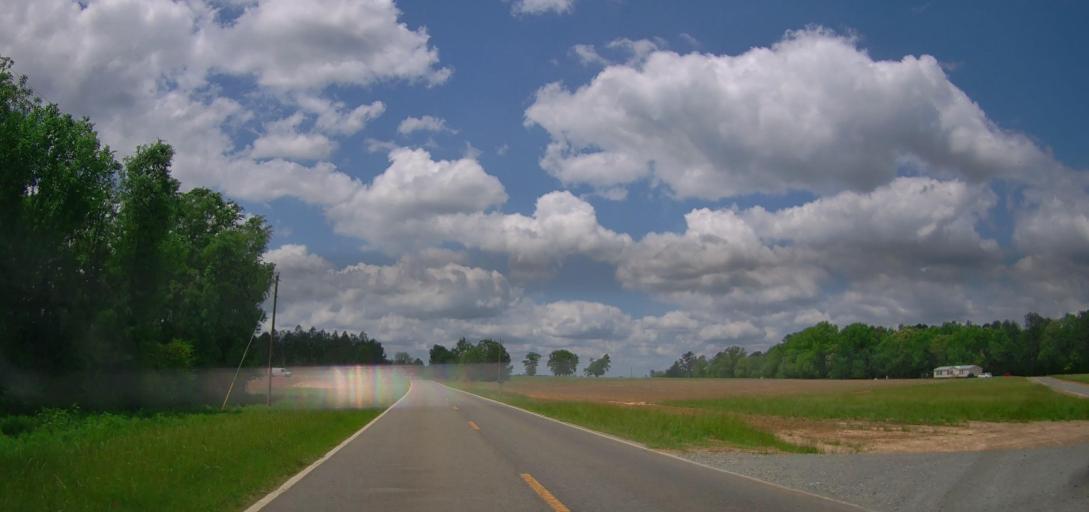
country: US
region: Georgia
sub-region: Laurens County
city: Dublin
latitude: 32.6025
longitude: -82.9897
